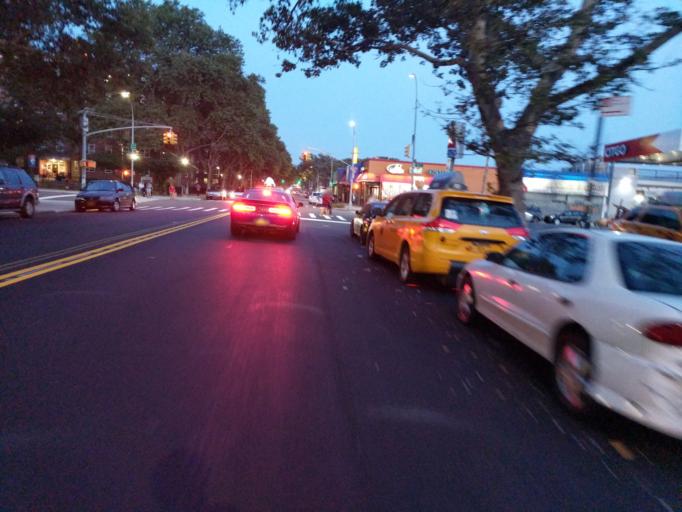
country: US
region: New York
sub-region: Queens County
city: Long Island City
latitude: 40.7601
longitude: -73.9373
